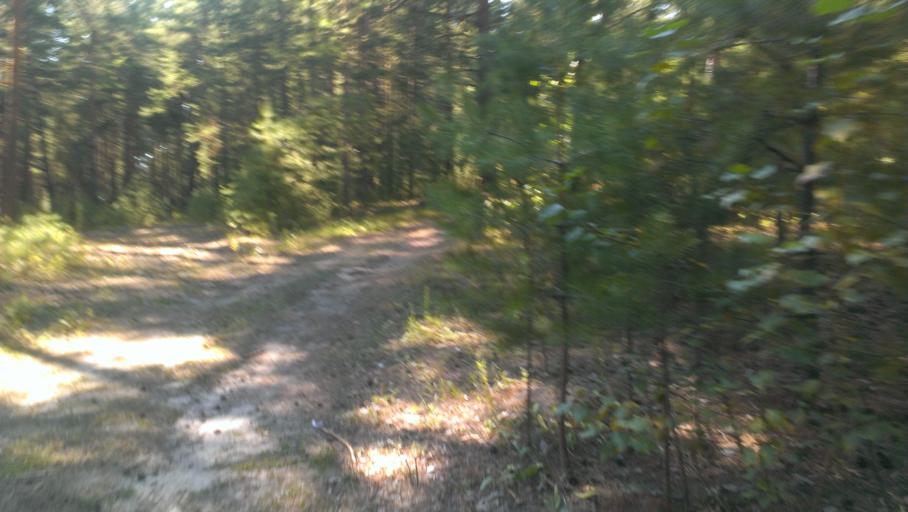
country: RU
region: Altai Krai
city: Yuzhnyy
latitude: 53.3148
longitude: 83.6853
